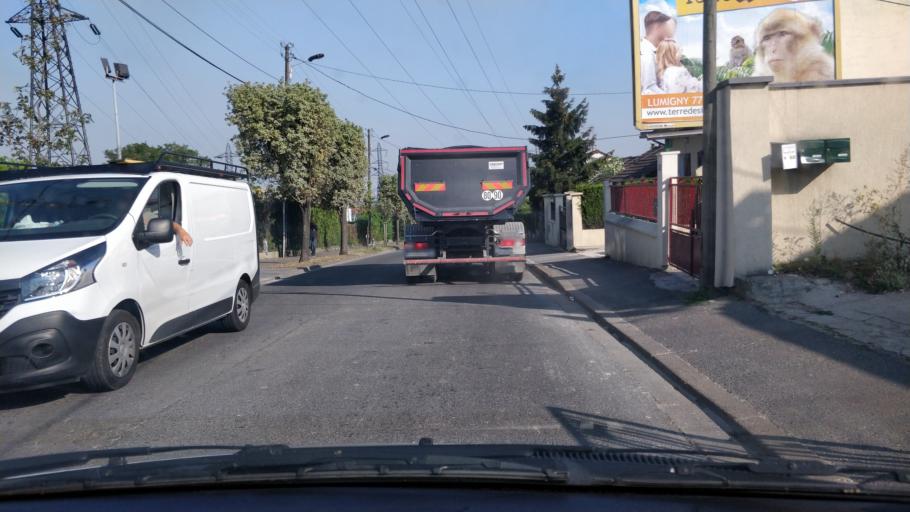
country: FR
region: Ile-de-France
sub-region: Departement de Seine-Saint-Denis
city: Villemomble
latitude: 48.8769
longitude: 2.4997
